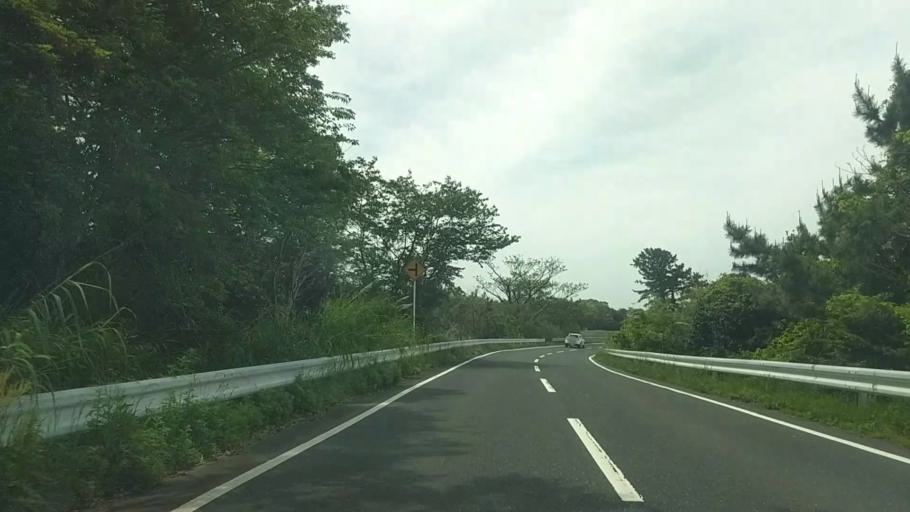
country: JP
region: Shizuoka
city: Kosai-shi
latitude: 34.7773
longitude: 137.5648
